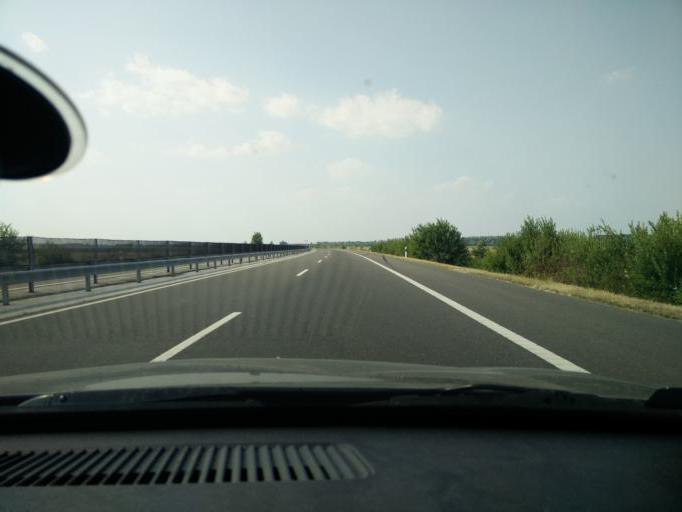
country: HU
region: Tolna
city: Ocseny
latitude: 46.3507
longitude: 18.7577
